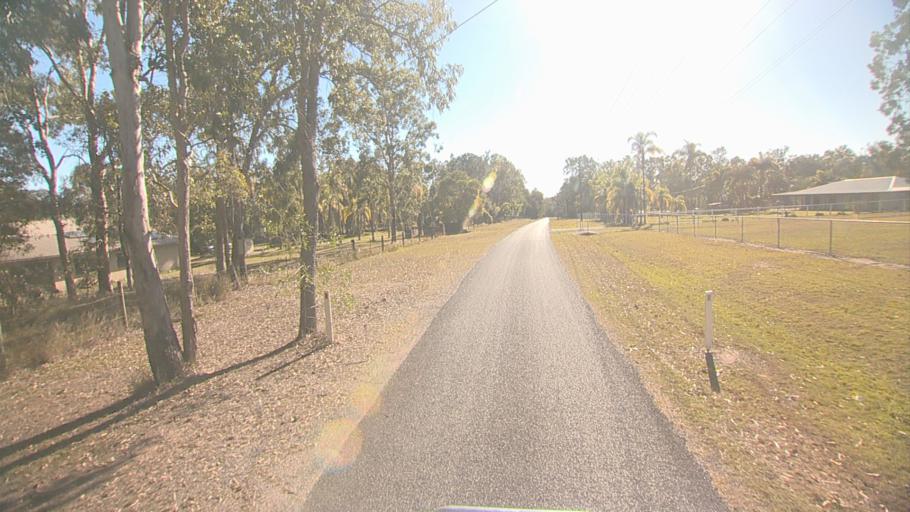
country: AU
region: Queensland
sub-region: Logan
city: Park Ridge South
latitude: -27.7514
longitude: 153.0474
